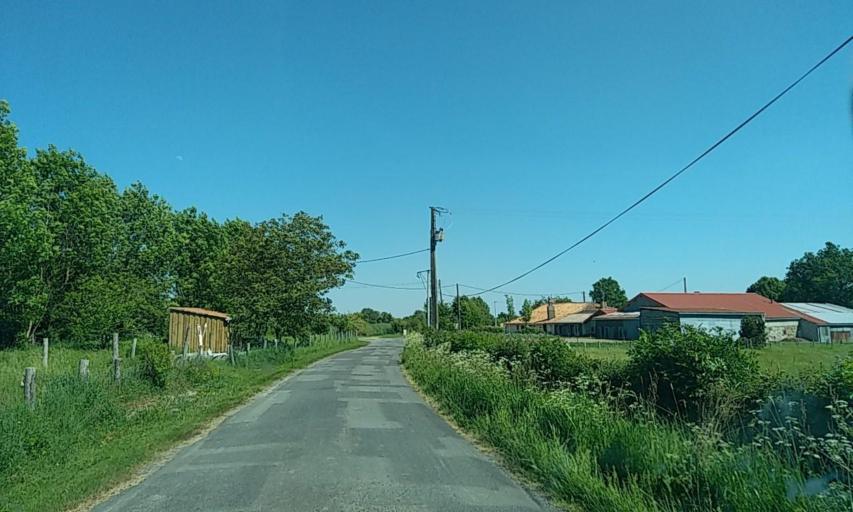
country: FR
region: Poitou-Charentes
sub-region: Departement des Deux-Sevres
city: La Chapelle-Saint-Laurent
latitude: 46.7697
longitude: -0.4671
